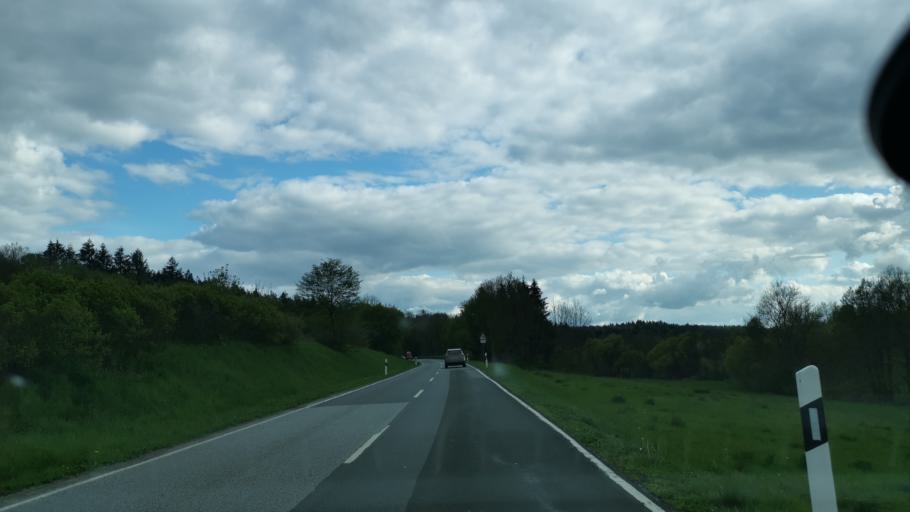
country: DE
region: Baden-Wuerttemberg
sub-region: Karlsruhe Region
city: Osterburken
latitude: 49.4663
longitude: 9.4155
